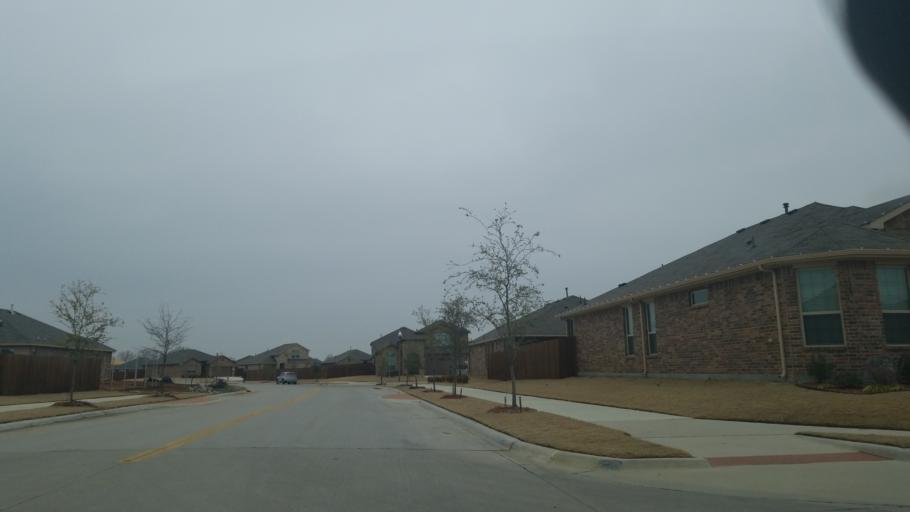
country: US
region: Texas
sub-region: Denton County
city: Denton
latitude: 33.1593
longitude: -97.1367
